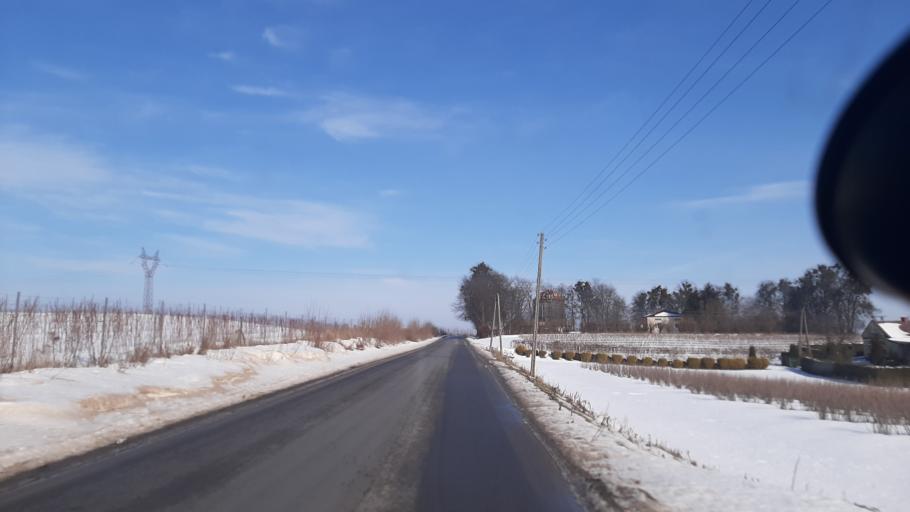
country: PL
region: Lublin Voivodeship
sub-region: Powiat pulawski
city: Wawolnica
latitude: 51.3490
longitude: 22.1116
